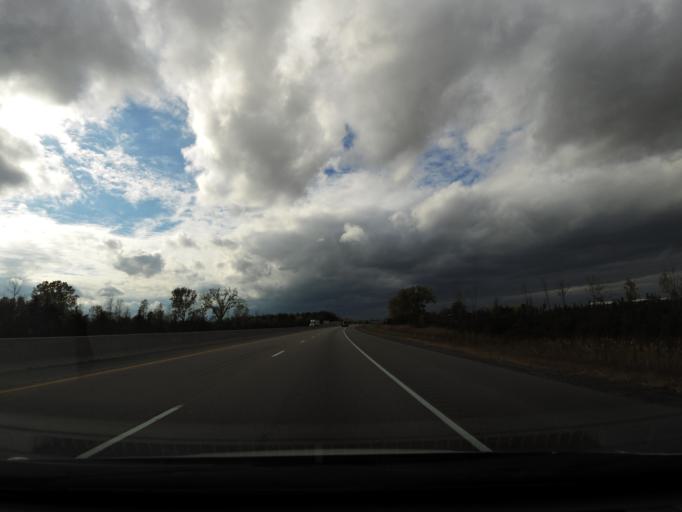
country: CA
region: Ontario
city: Belleville
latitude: 44.2176
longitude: -77.2671
